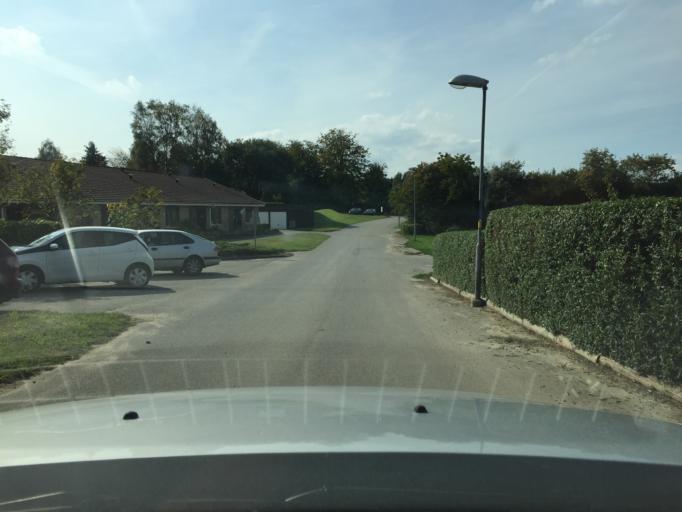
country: SE
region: Skane
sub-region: Kristianstads Kommun
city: Degeberga
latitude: 55.7255
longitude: 14.1113
